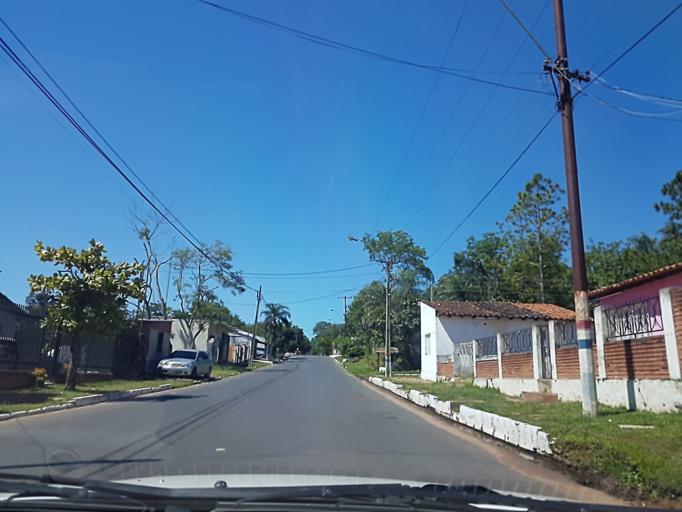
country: PY
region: Cordillera
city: Atyra
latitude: -25.2814
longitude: -57.1752
